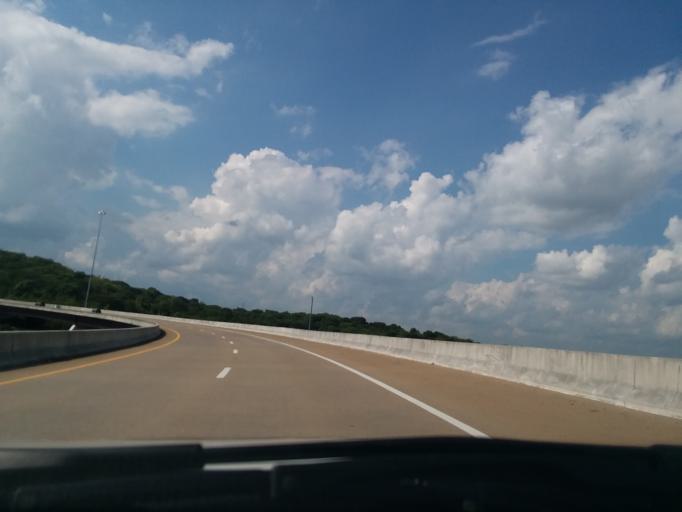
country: US
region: Tennessee
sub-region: Davidson County
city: Nashville
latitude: 36.2377
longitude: -86.7426
